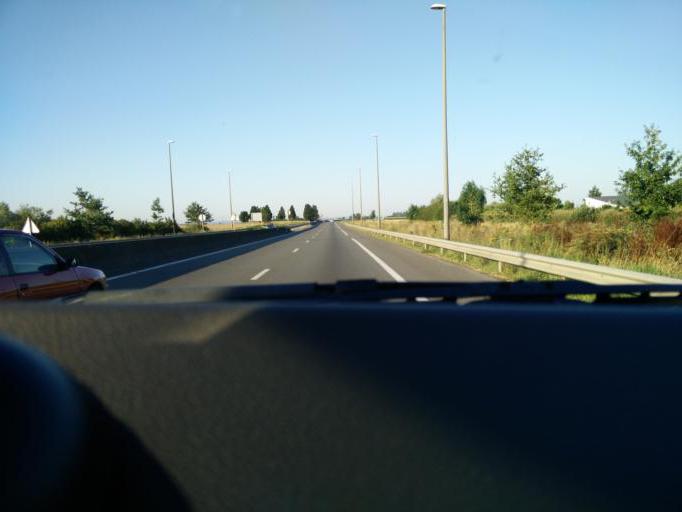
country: FR
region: Nord-Pas-de-Calais
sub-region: Departement du Nord
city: Herlies
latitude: 50.5683
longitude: 2.8536
